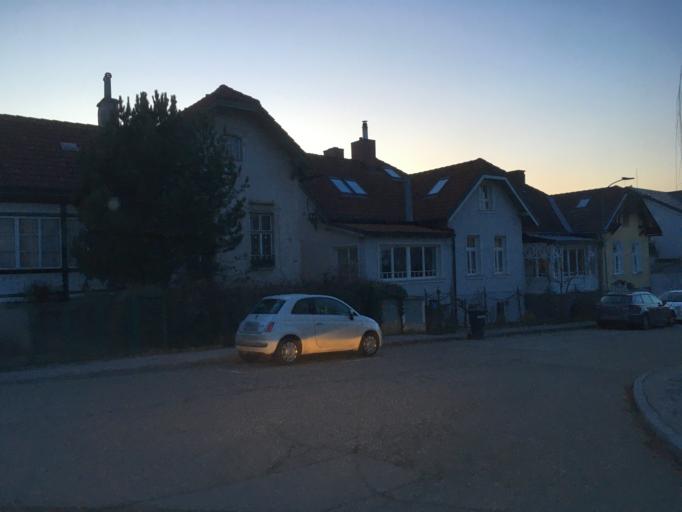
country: AT
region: Lower Austria
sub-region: Politischer Bezirk Tulln
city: Wordern
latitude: 48.3268
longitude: 16.2177
